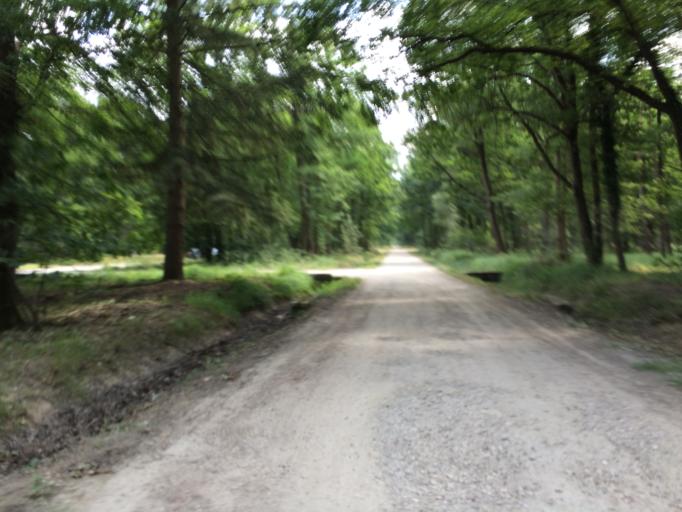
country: FR
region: Ile-de-France
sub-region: Departement de l'Essonne
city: Brunoy
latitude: 48.6775
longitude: 2.4891
